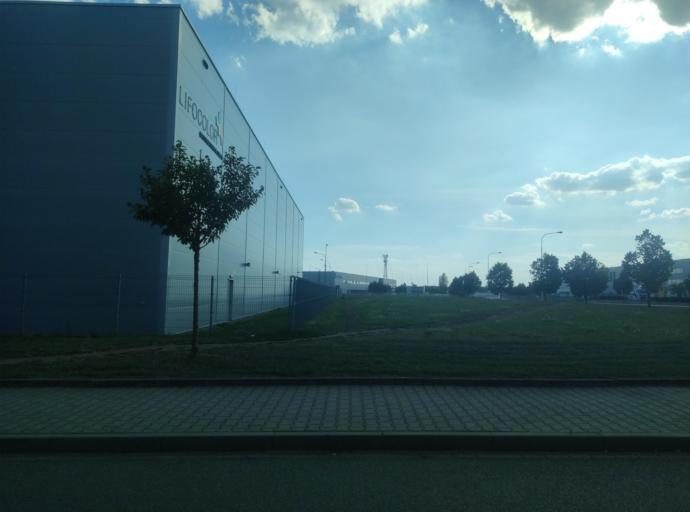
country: CZ
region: South Moravian
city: Podoli
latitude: 49.1750
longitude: 16.6694
